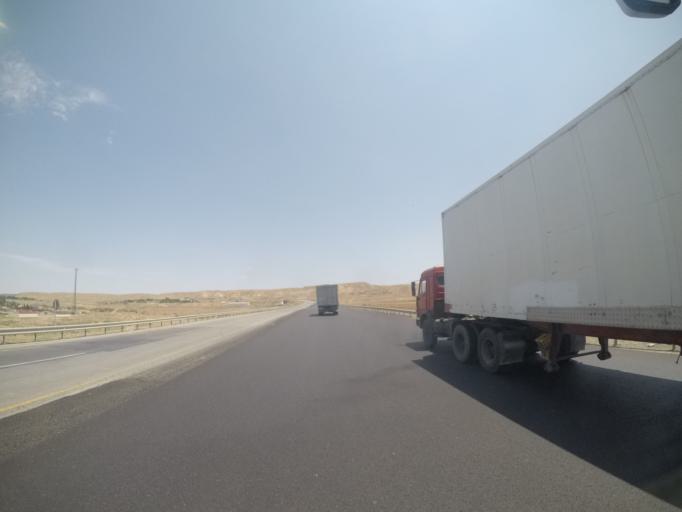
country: AZ
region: Haciqabul
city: Haciqabul
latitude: 40.0156
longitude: 48.9453
